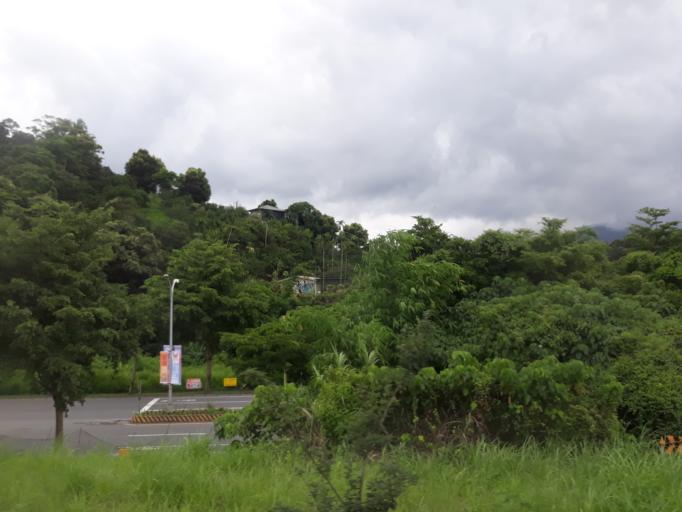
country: TW
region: Taiwan
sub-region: Yilan
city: Yilan
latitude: 24.6152
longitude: 121.8149
